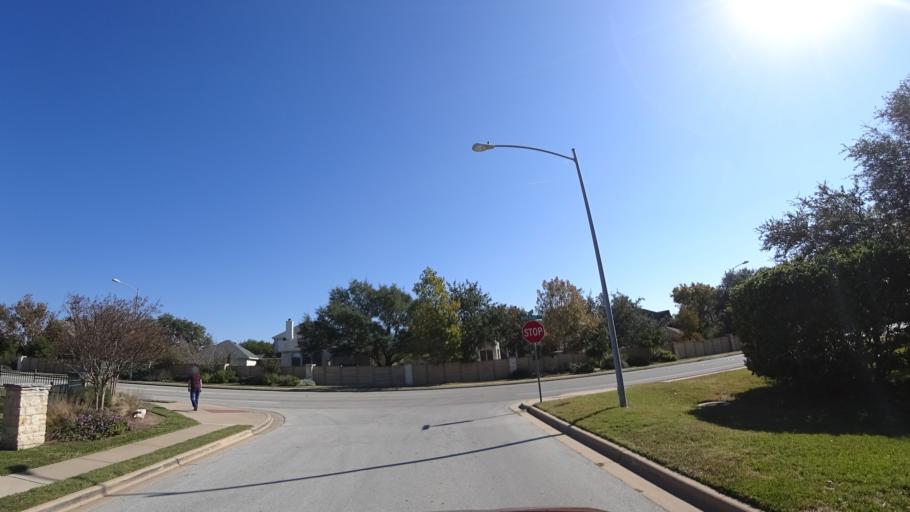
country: US
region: Texas
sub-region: Travis County
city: Lost Creek
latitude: 30.3772
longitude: -97.8532
